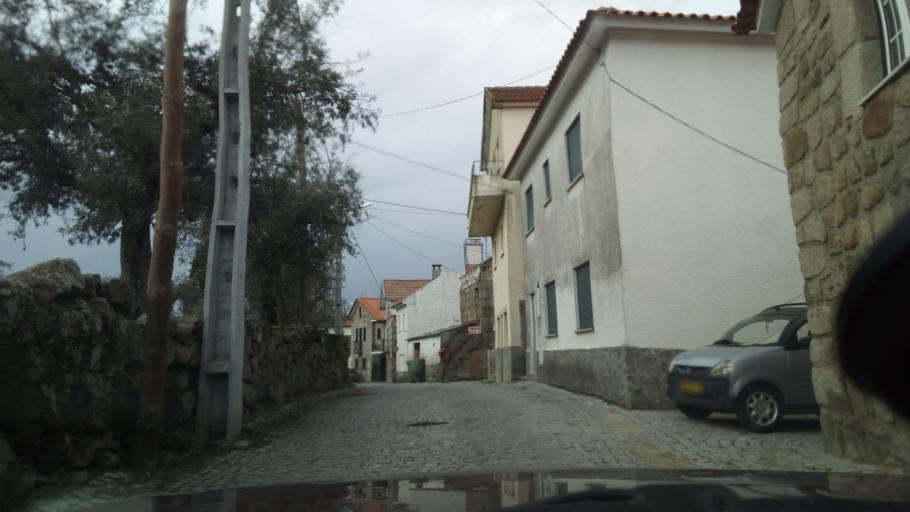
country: PT
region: Guarda
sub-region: Fornos de Algodres
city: Fornos de Algodres
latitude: 40.5806
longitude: -7.4727
